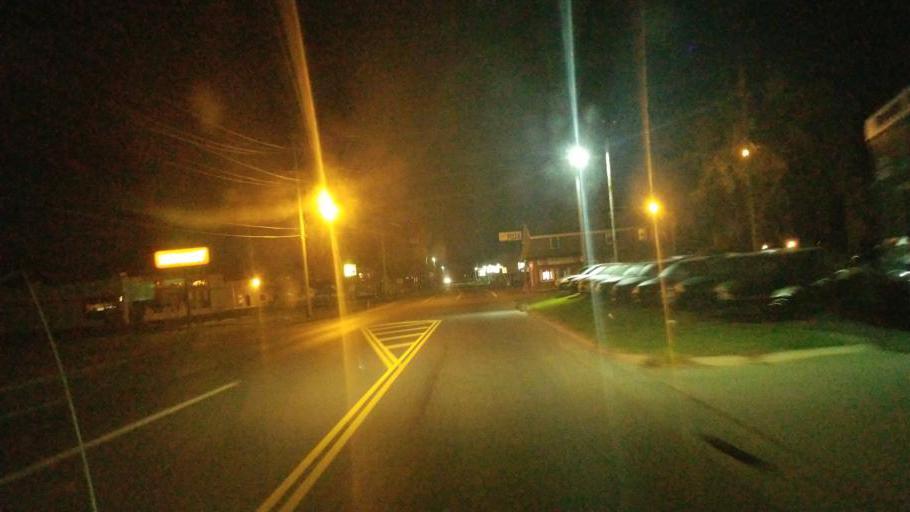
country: US
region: Ohio
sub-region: Licking County
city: Newark
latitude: 40.0869
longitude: -82.4184
